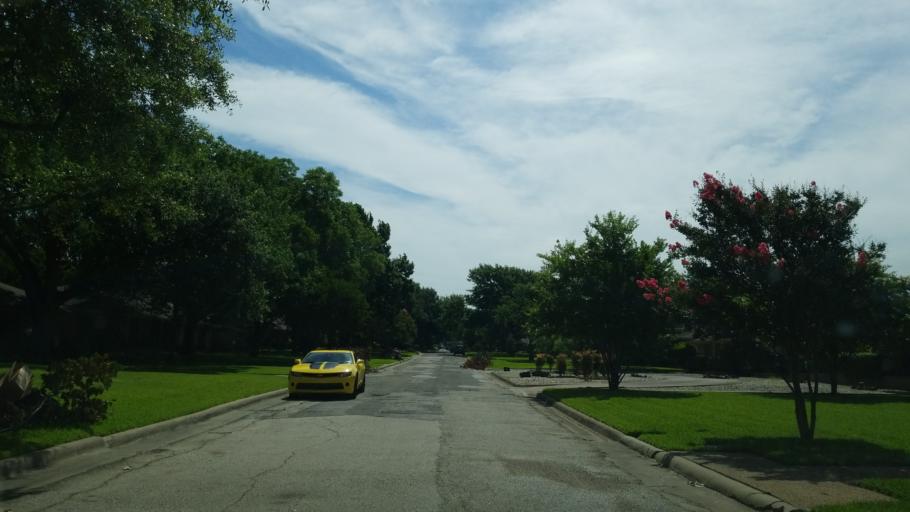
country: US
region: Texas
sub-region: Dallas County
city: Farmers Branch
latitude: 32.9064
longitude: -96.8551
